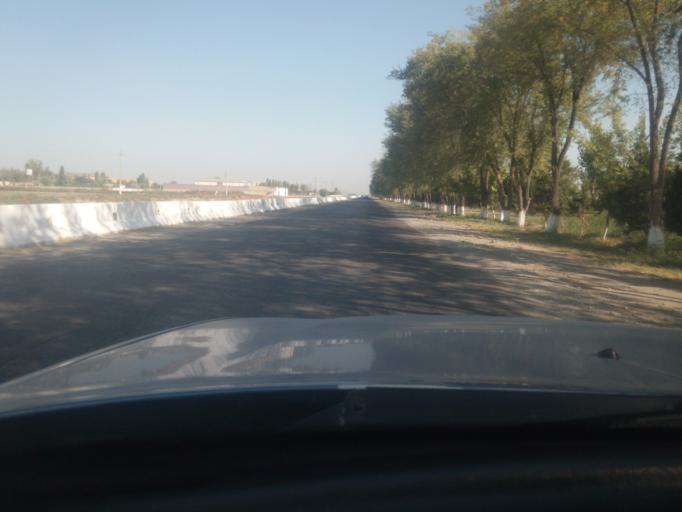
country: UZ
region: Sirdaryo
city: Guliston
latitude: 40.5119
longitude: 68.7950
